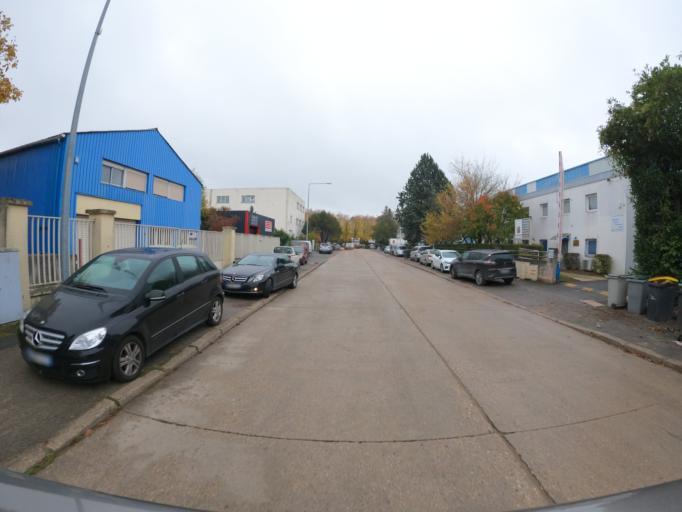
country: FR
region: Ile-de-France
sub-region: Departement du Val-de-Marne
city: Chennevieres-sur-Marne
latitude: 48.7935
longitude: 2.5454
